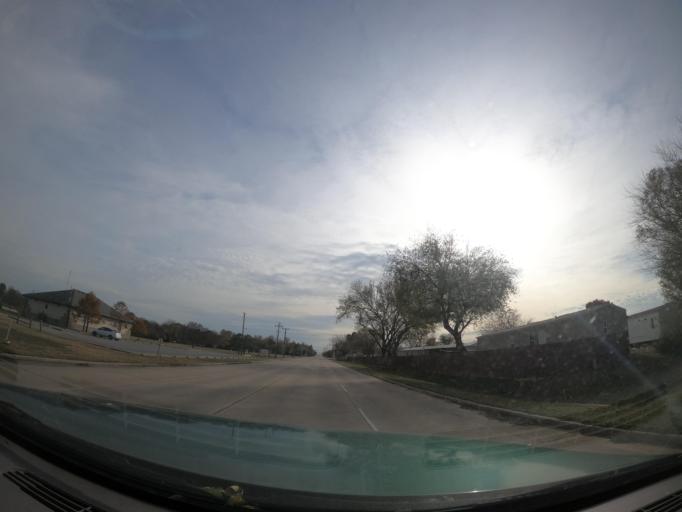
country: US
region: Oklahoma
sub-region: Tulsa County
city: Turley
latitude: 36.2448
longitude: -95.9584
